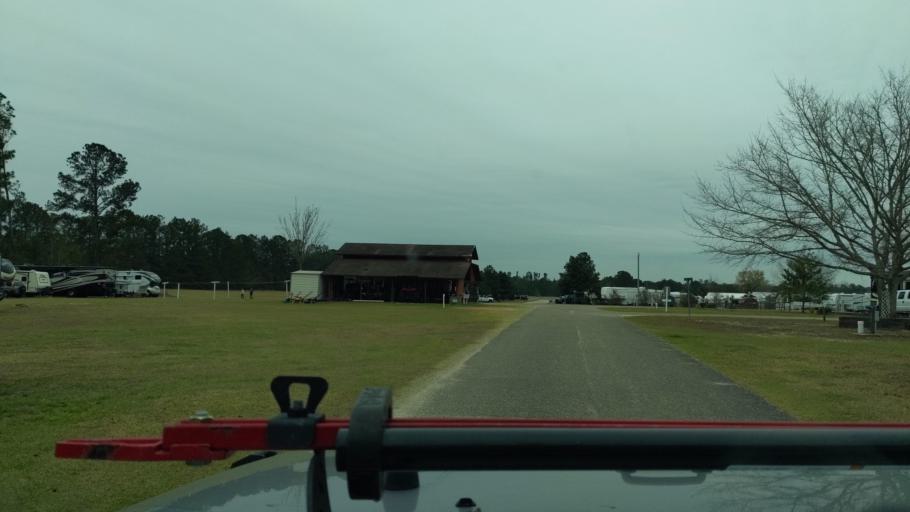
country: US
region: Alabama
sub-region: Baldwin County
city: Foley
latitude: 30.4586
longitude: -87.7834
